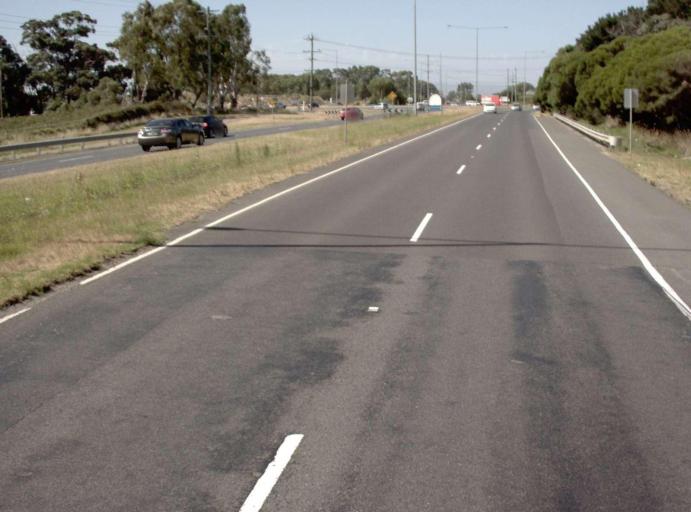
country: AU
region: Victoria
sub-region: Frankston
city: Sandhurst
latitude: -38.0738
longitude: 145.1936
